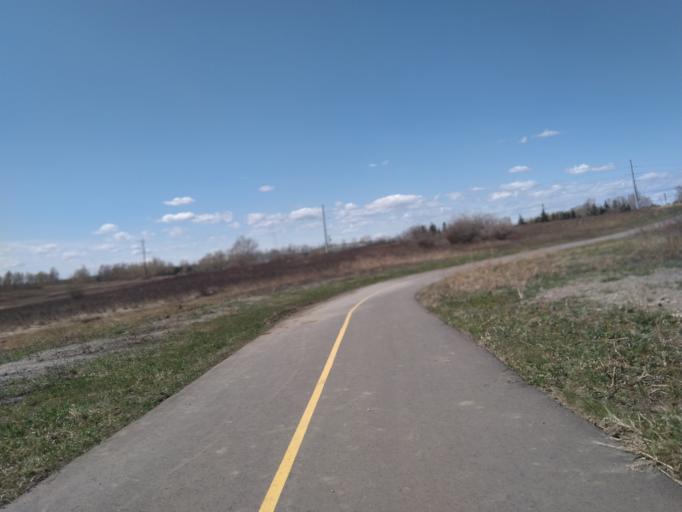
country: CA
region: Alberta
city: Chestermere
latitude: 51.0368
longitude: -113.9313
